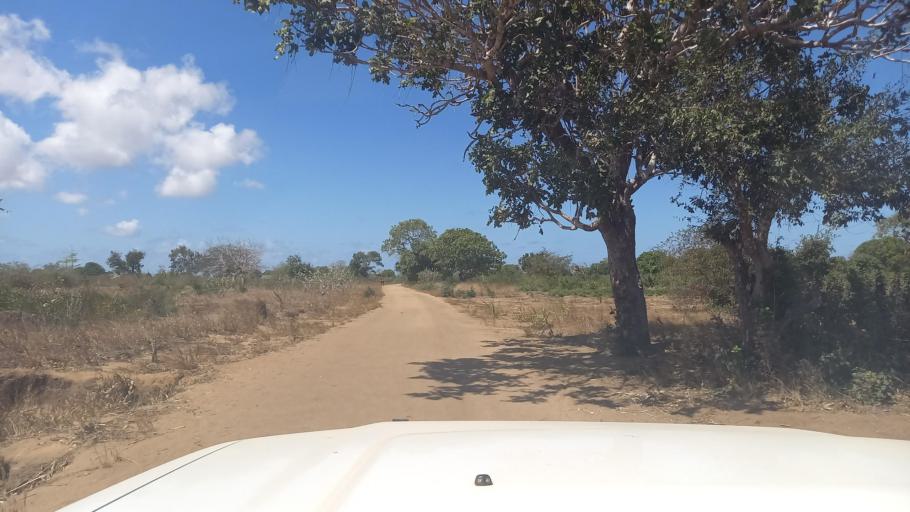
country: MZ
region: Cabo Delgado
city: Pemba
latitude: -13.4227
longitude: 40.5052
